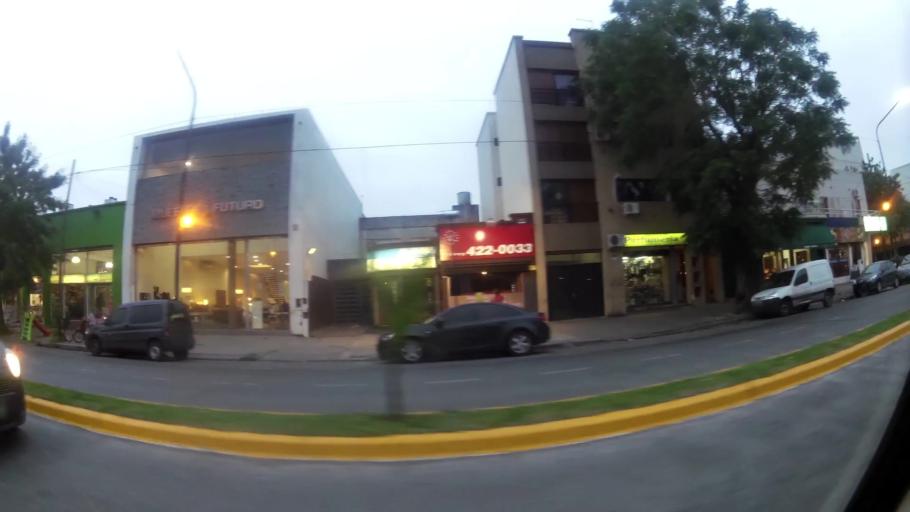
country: AR
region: Buenos Aires
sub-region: Partido de La Plata
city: La Plata
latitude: -34.9136
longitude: -57.9652
